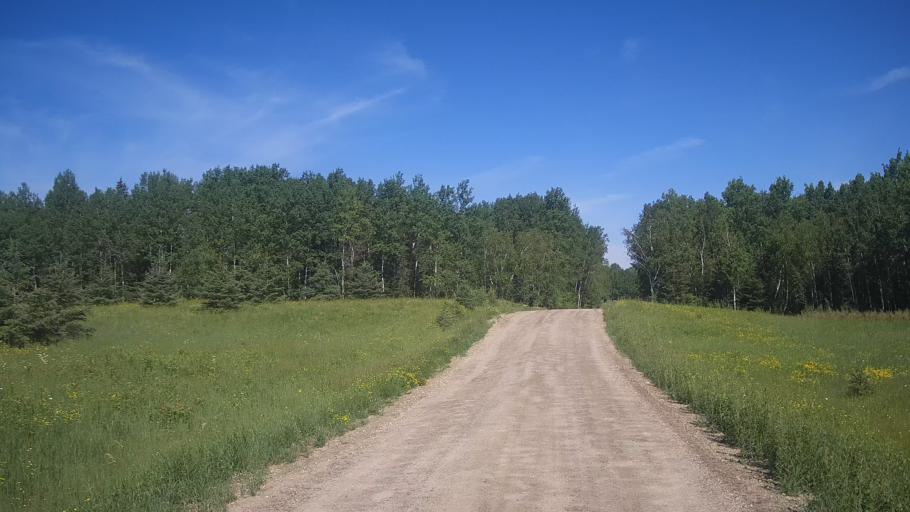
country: CA
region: Ontario
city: Dryden
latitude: 49.8197
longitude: -93.3367
